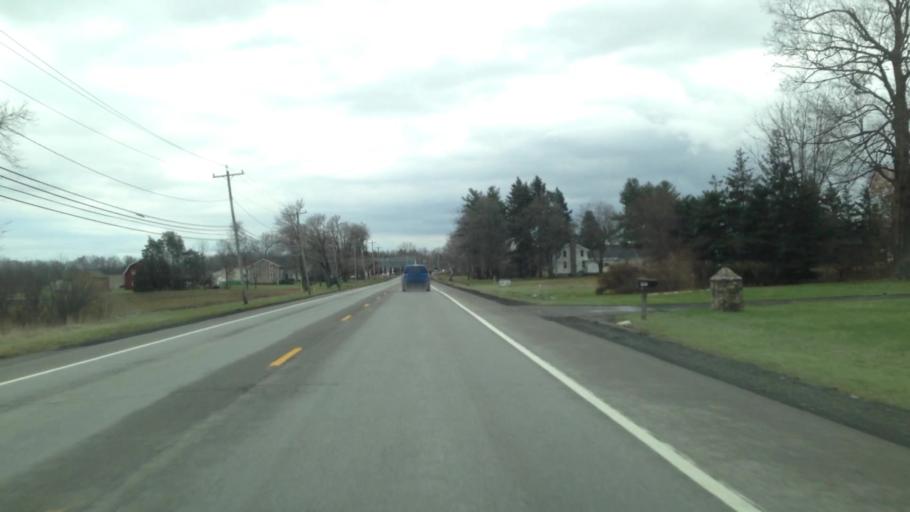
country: US
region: New York
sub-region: Erie County
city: Akron
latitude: 42.9981
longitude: -78.4980
